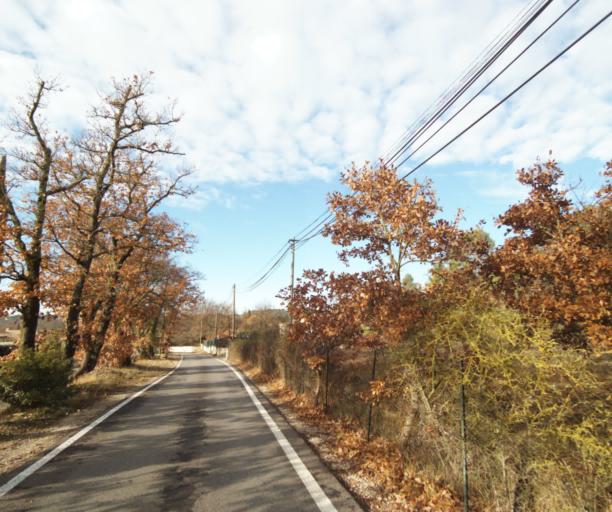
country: FR
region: Provence-Alpes-Cote d'Azur
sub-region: Departement du Var
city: Trans-en-Provence
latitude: 43.4909
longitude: 6.4799
